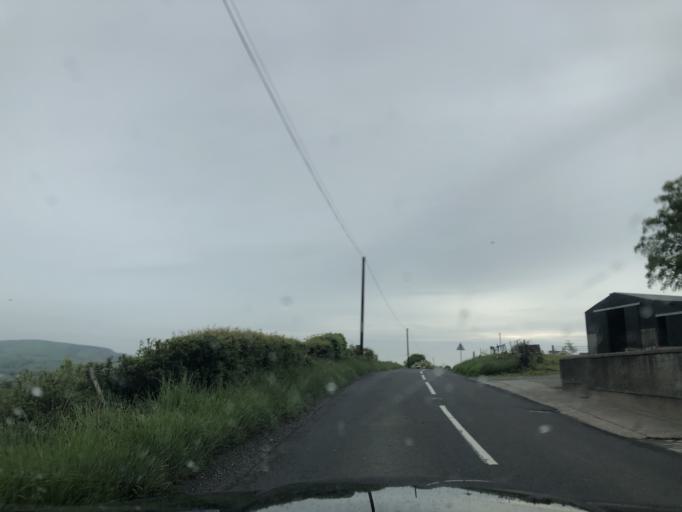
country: GB
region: Northern Ireland
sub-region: Down District
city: Castlewellan
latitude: 54.2207
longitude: -6.0184
